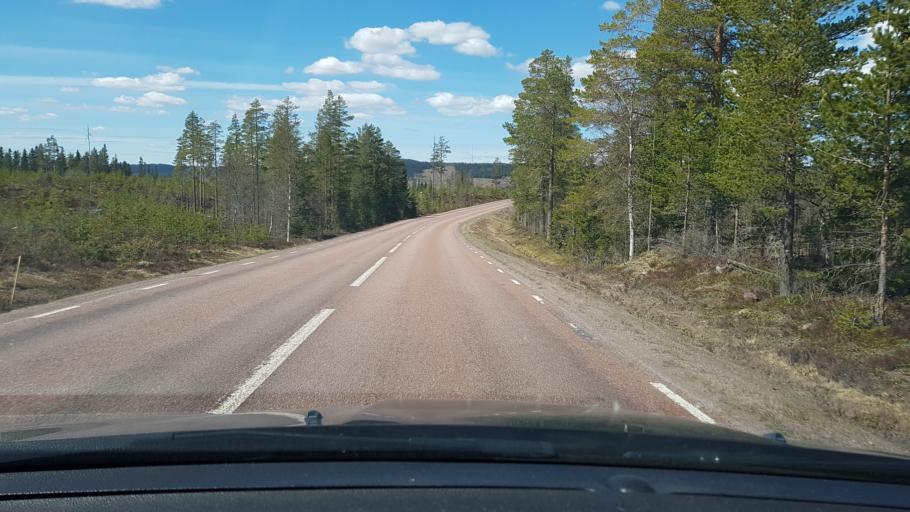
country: SE
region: Dalarna
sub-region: Malung-Saelens kommun
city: Malung
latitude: 61.0484
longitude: 13.3756
